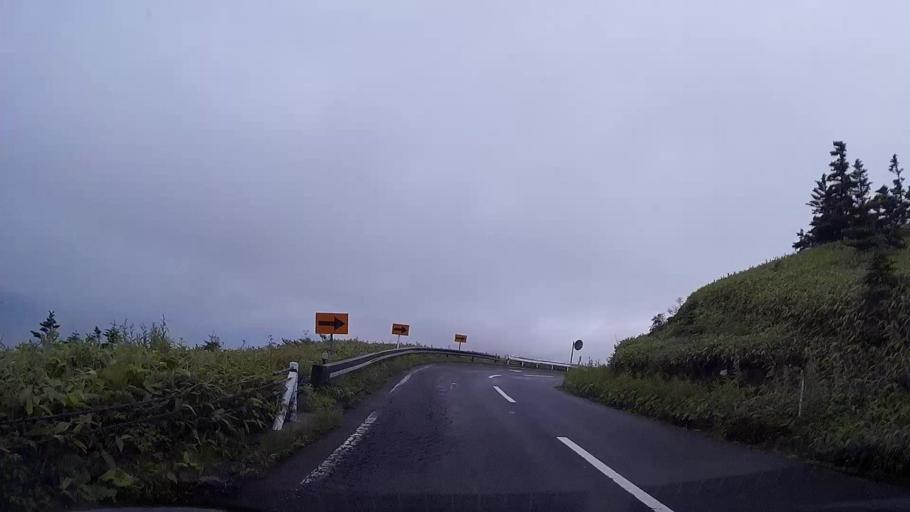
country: JP
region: Nagano
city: Nakano
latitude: 36.6589
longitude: 138.5341
